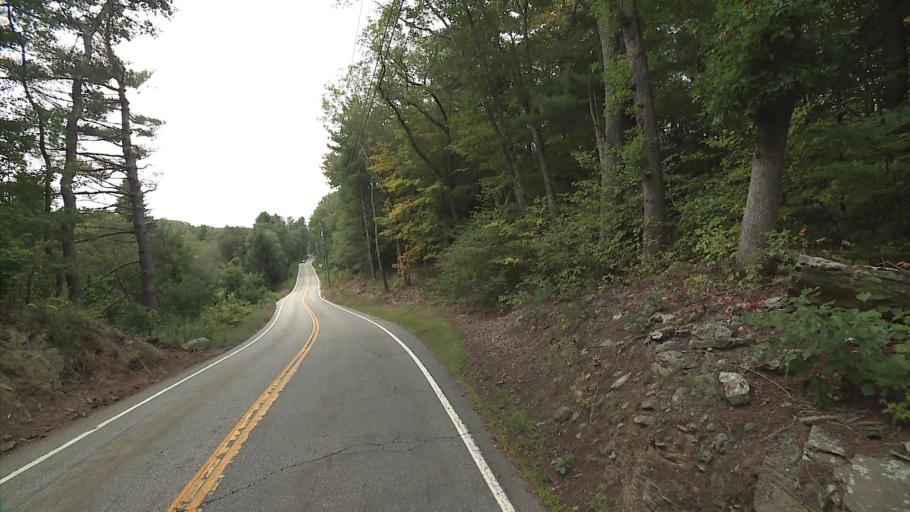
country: US
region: Connecticut
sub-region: Tolland County
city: Stafford Springs
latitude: 41.9023
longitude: -72.2673
